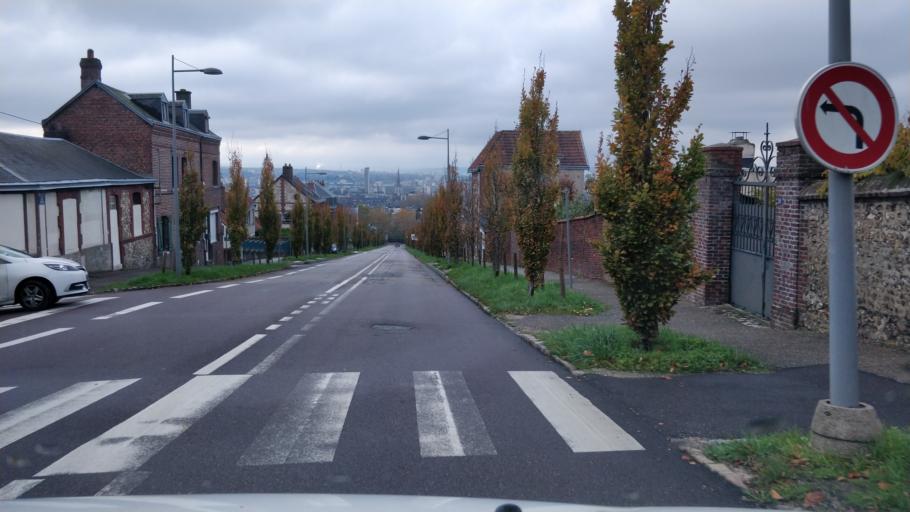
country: FR
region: Haute-Normandie
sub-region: Departement de la Seine-Maritime
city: Bihorel
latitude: 49.4485
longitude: 1.1126
